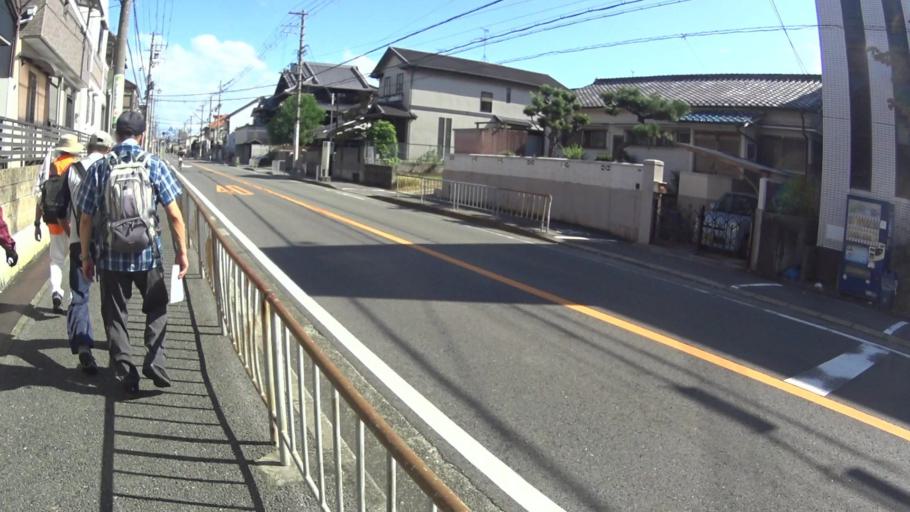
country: JP
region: Ehime
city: Kihoku-cho
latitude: 33.3745
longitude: 132.8066
